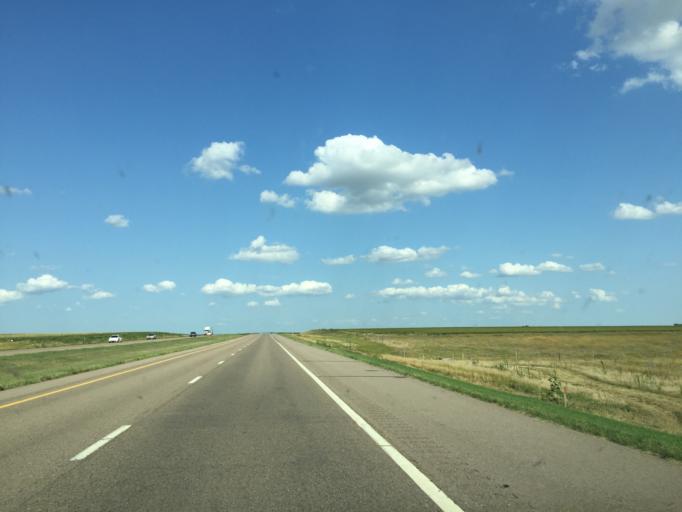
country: US
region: Kansas
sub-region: Trego County
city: WaKeeney
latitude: 39.0231
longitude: -100.0582
